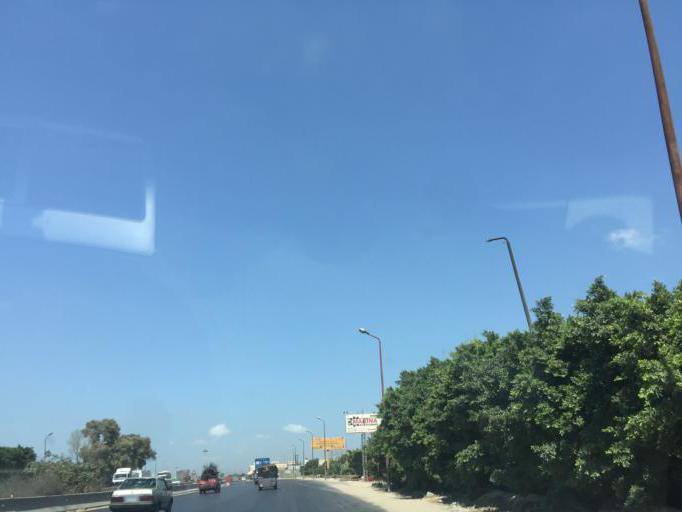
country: EG
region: Alexandria
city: Alexandria
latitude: 31.0757
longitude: 29.8374
